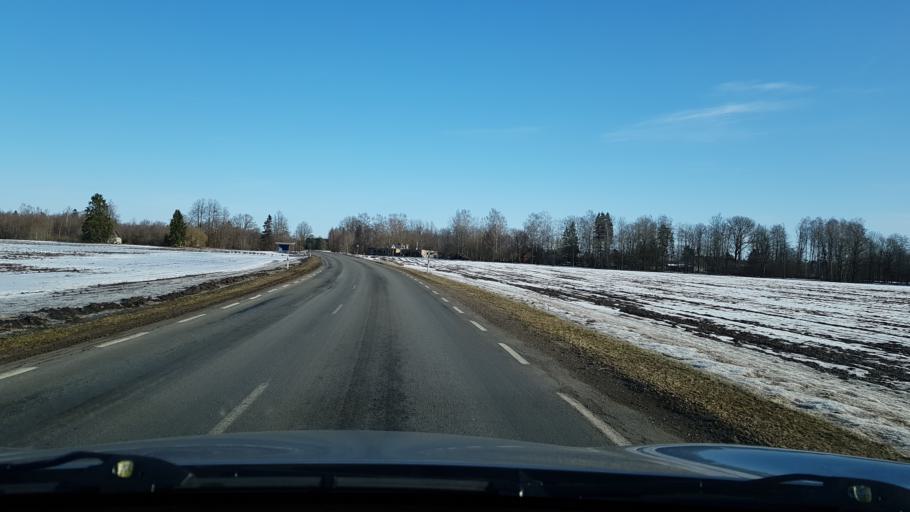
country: EE
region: Viljandimaa
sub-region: Vohma linn
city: Vohma
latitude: 58.6314
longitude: 25.6414
